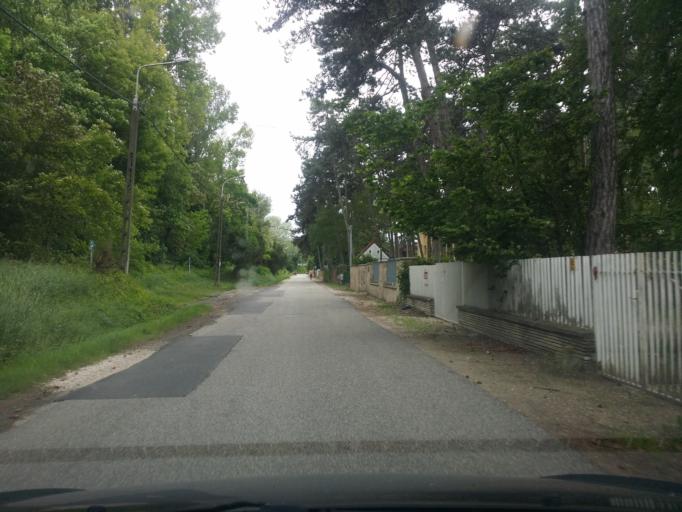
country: HU
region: Somogy
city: Balatonszabadi
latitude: 46.9580
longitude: 18.1521
